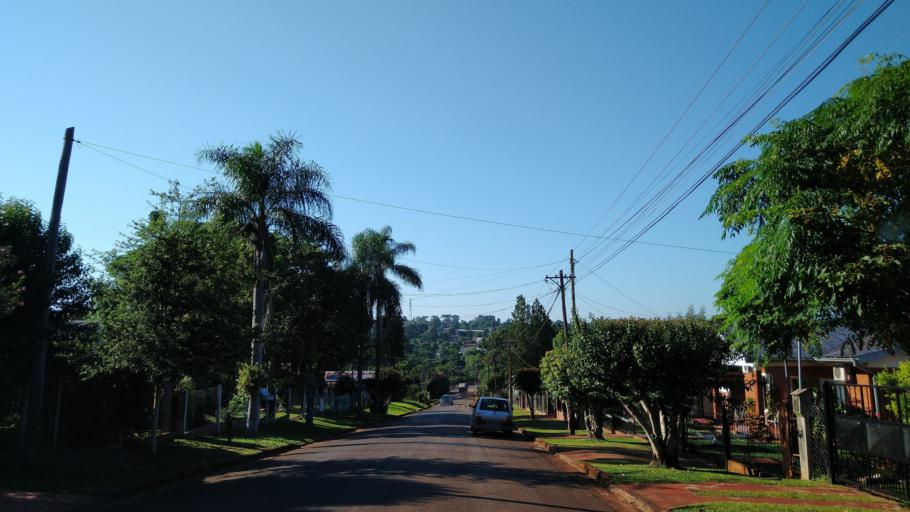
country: AR
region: Misiones
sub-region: Departamento de Montecarlo
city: Montecarlo
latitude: -26.5607
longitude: -54.7733
